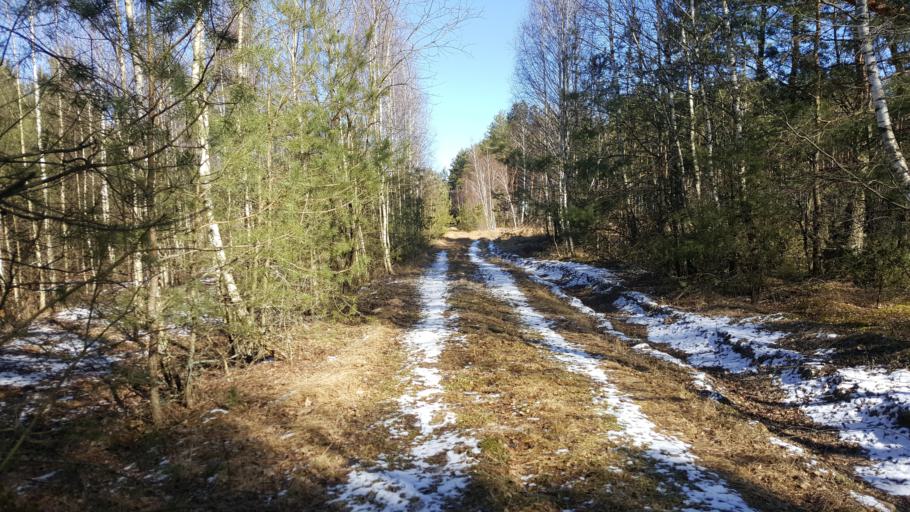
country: BY
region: Brest
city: Kamyanyets
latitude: 52.3674
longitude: 23.8212
